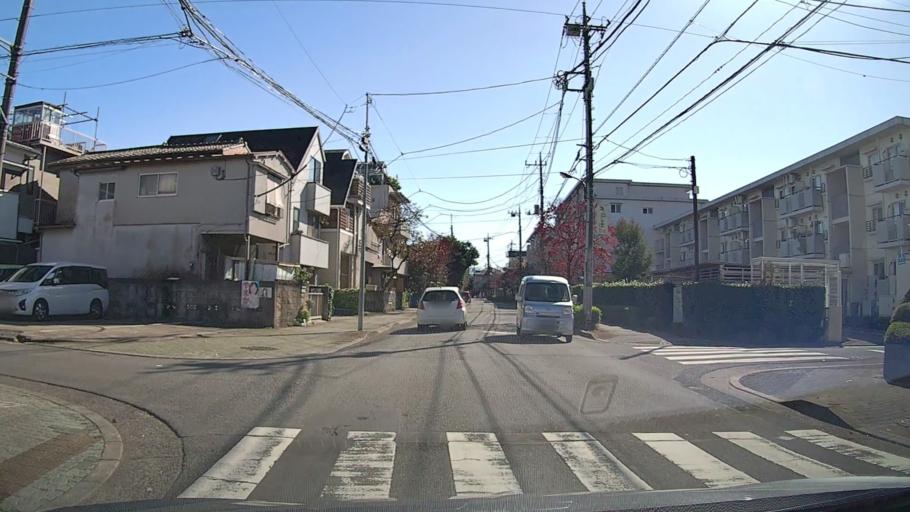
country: JP
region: Saitama
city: Wako
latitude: 35.7522
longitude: 139.6252
